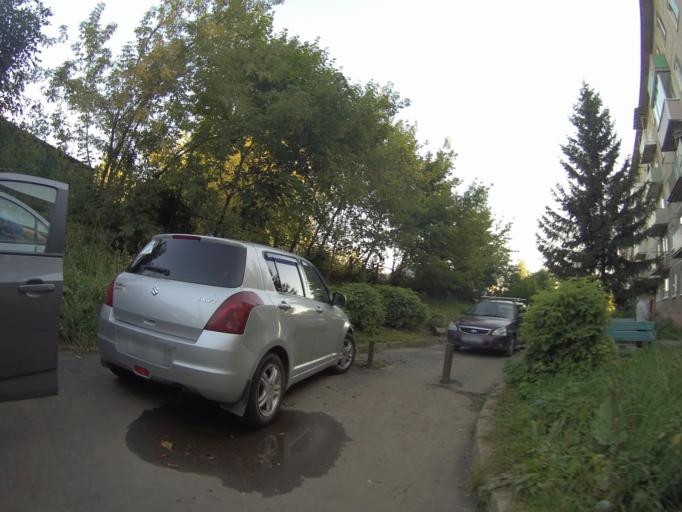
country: RU
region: Vladimir
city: Vladimir
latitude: 56.1472
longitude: 40.3636
